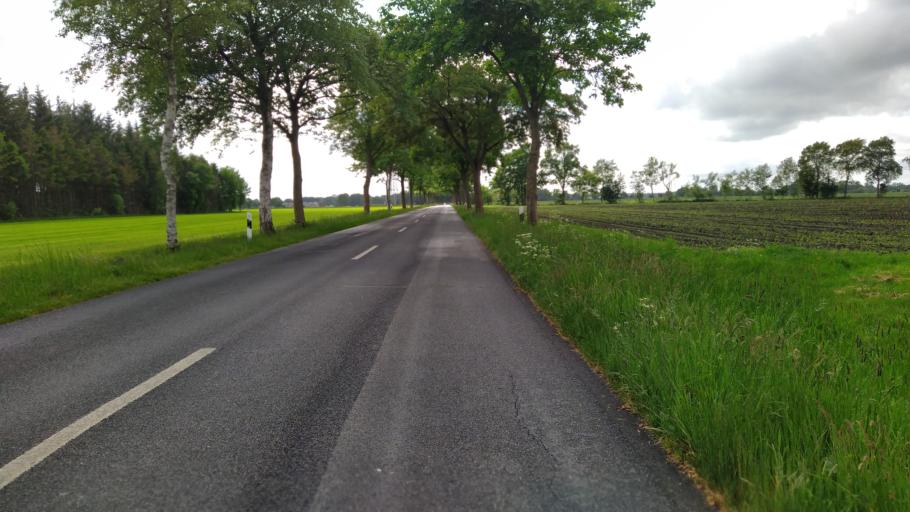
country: DE
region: Lower Saxony
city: Brest
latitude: 53.4532
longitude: 9.4055
